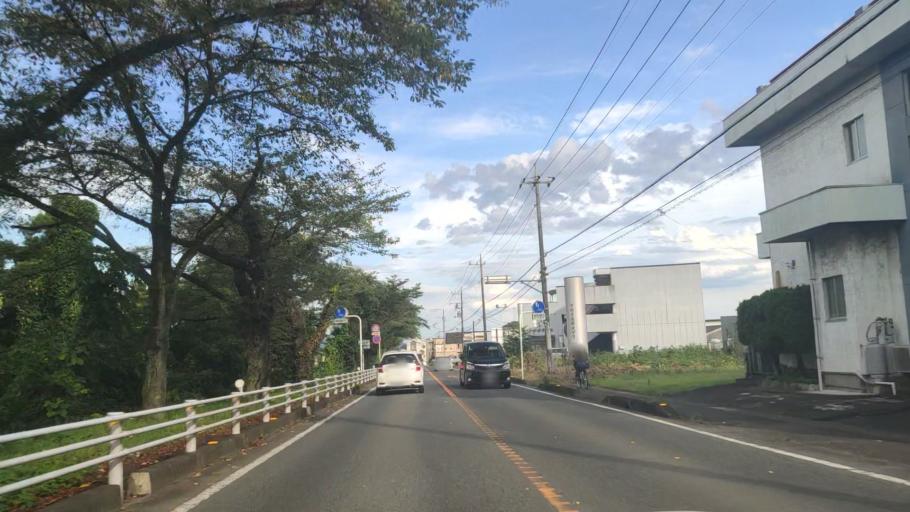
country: JP
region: Gunma
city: Omamacho-omama
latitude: 36.4278
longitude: 139.2852
